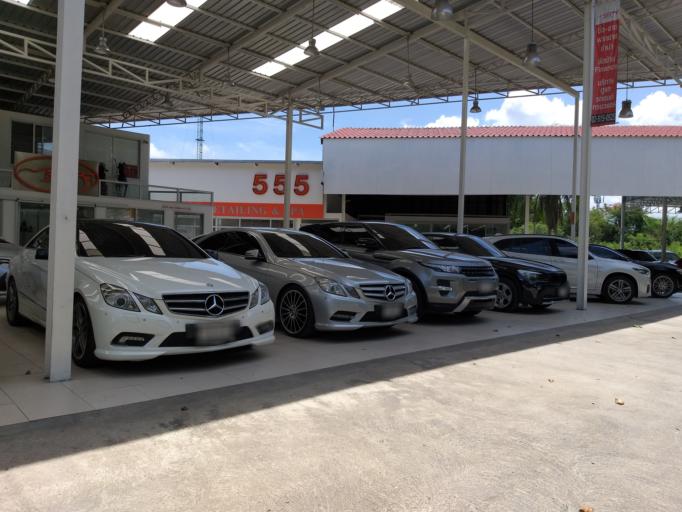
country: TH
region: Bangkok
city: Lat Phrao
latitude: 13.8168
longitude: 100.6228
